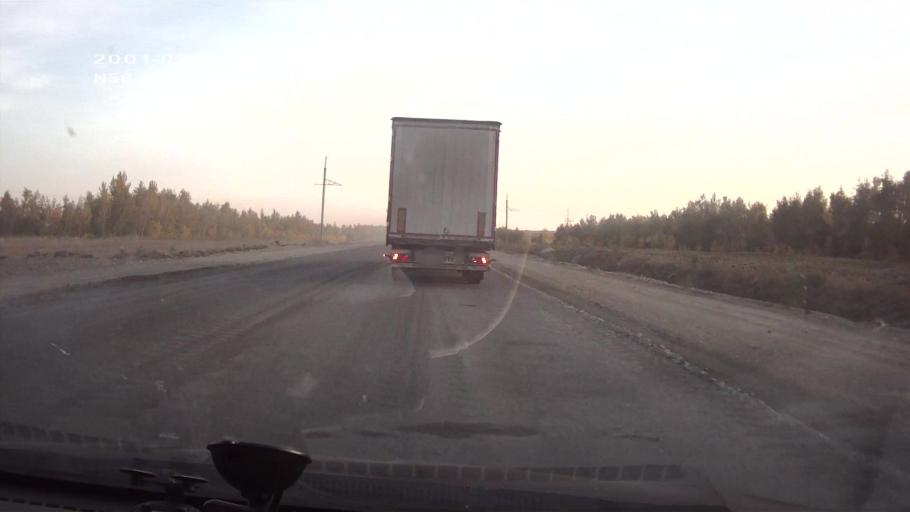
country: RU
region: Saratov
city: Kamenskiy
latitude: 50.9239
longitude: 45.5987
